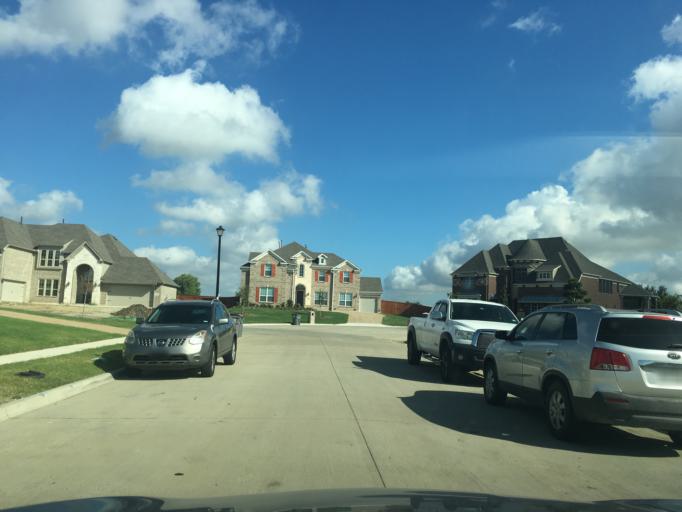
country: US
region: Texas
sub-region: Dallas County
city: Sachse
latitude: 32.9703
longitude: -96.5751
